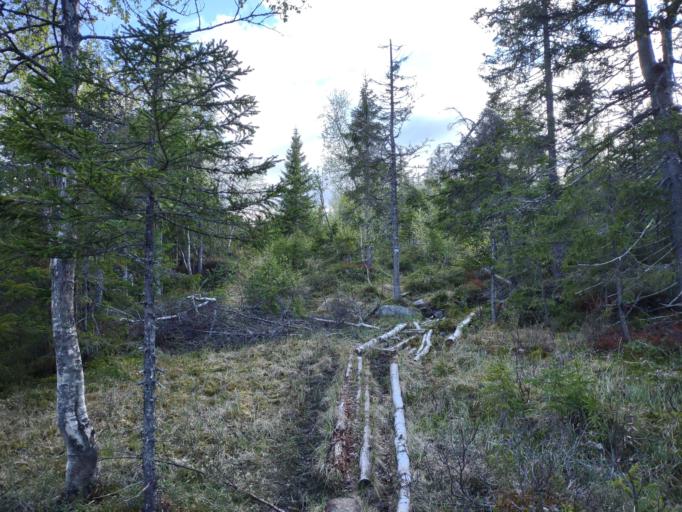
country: NO
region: Akershus
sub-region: Nittedal
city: Aneby
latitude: 60.2556
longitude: 10.8415
